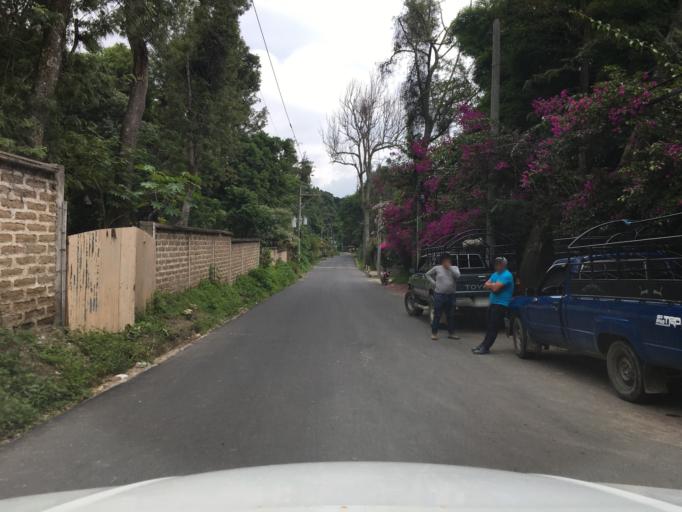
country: GT
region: Solola
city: Panajachel
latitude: 14.7360
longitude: -91.1486
